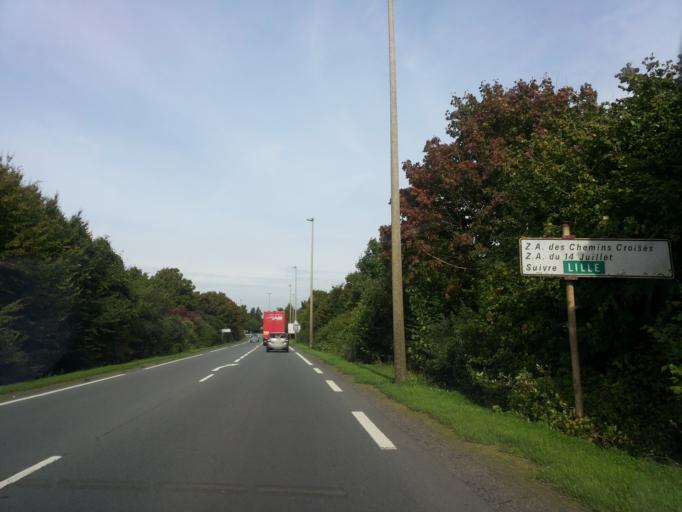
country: FR
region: Nord-Pas-de-Calais
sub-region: Departement du Pas-de-Calais
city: Saint-Laurent-Blangy
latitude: 50.2856
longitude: 2.8037
